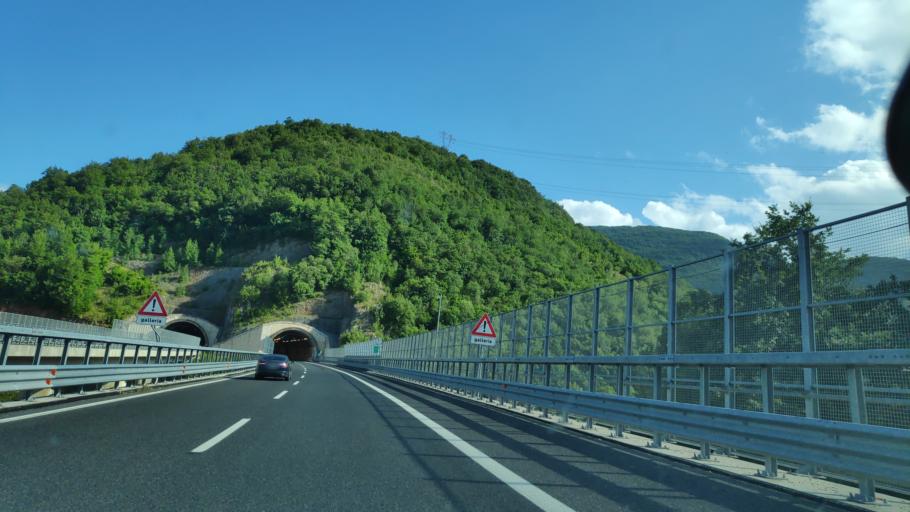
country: IT
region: Campania
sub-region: Provincia di Salerno
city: Casalbuono
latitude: 40.2151
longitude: 15.6723
